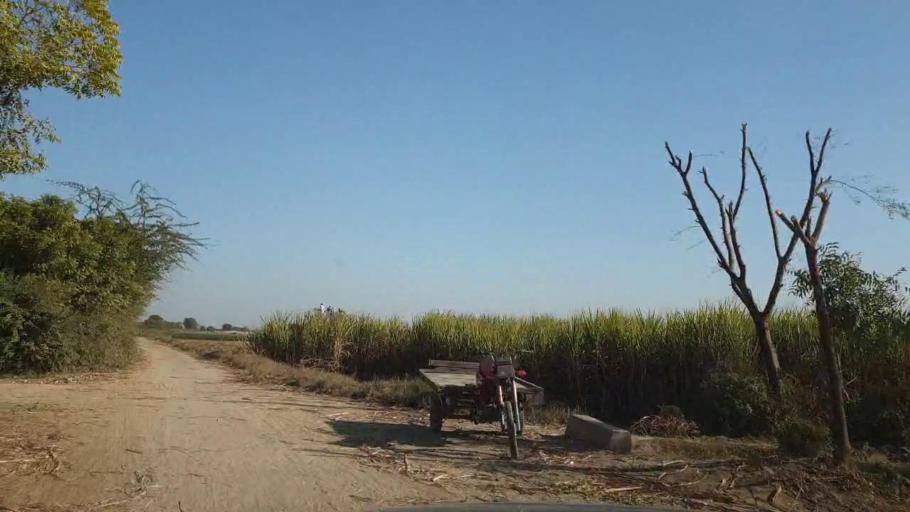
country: PK
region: Sindh
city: Tando Adam
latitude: 25.6855
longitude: 68.6881
